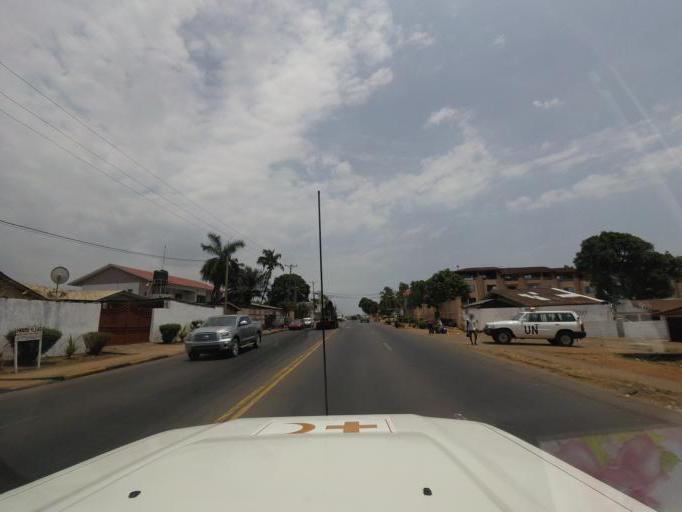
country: LR
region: Montserrado
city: Monrovia
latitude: 6.2663
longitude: -10.7211
